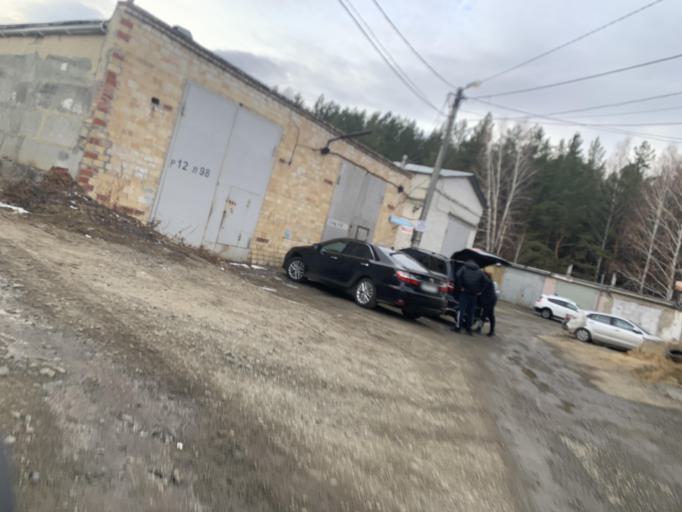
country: RU
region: Chelyabinsk
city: Roshchino
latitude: 55.1959
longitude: 61.2786
